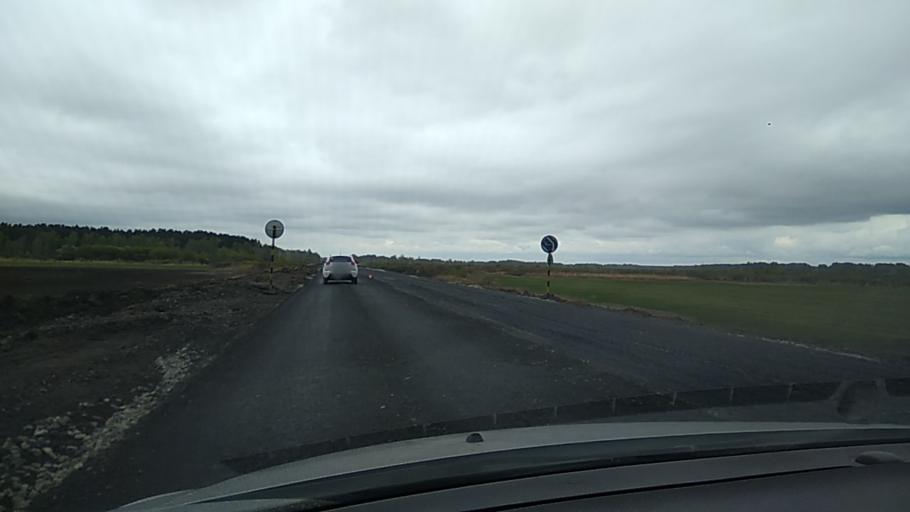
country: RU
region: Kurgan
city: Shadrinsk
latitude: 56.1529
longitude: 63.4243
